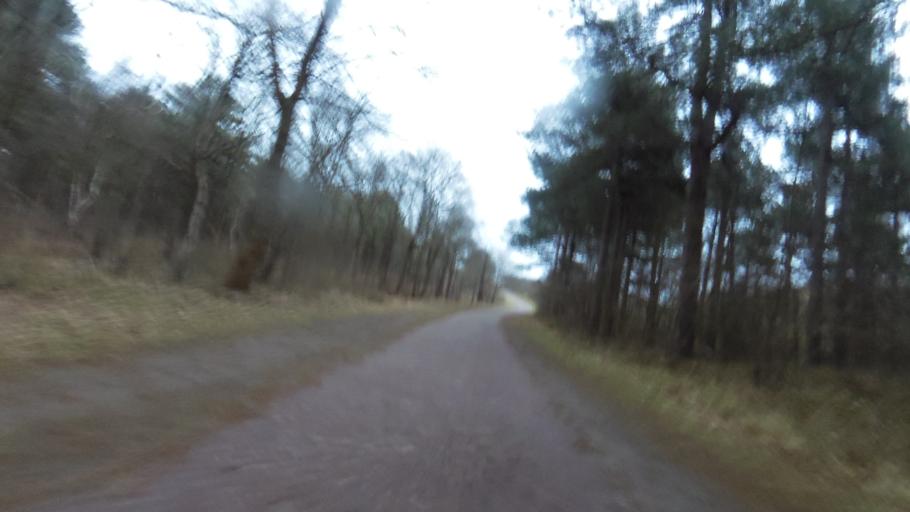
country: NL
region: North Holland
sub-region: Gemeente Bergen
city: Egmond aan Zee
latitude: 52.5959
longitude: 4.6283
